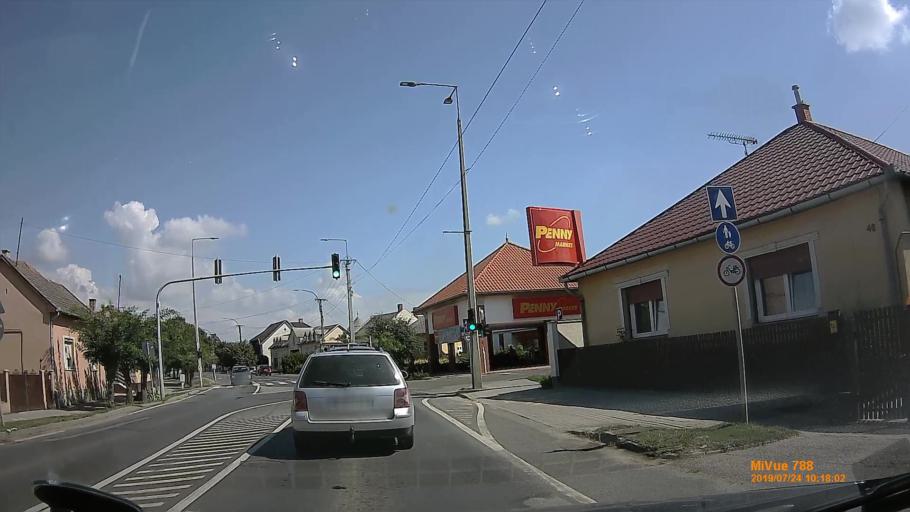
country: HU
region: Szabolcs-Szatmar-Bereg
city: Vasarosnameny
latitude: 48.1244
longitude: 22.3183
